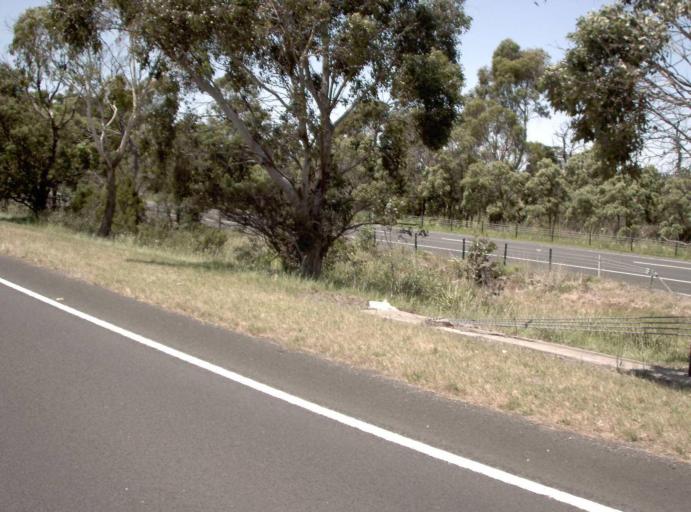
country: AU
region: Victoria
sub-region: Cardinia
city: Pakenham Upper
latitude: -38.0696
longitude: 145.5768
